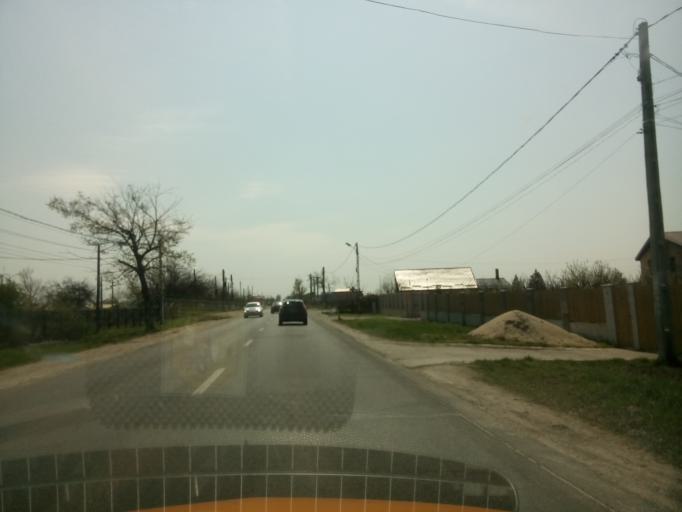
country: RO
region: Calarasi
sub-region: Comuna Frumusani
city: Frumusani
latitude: 44.2927
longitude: 26.3170
